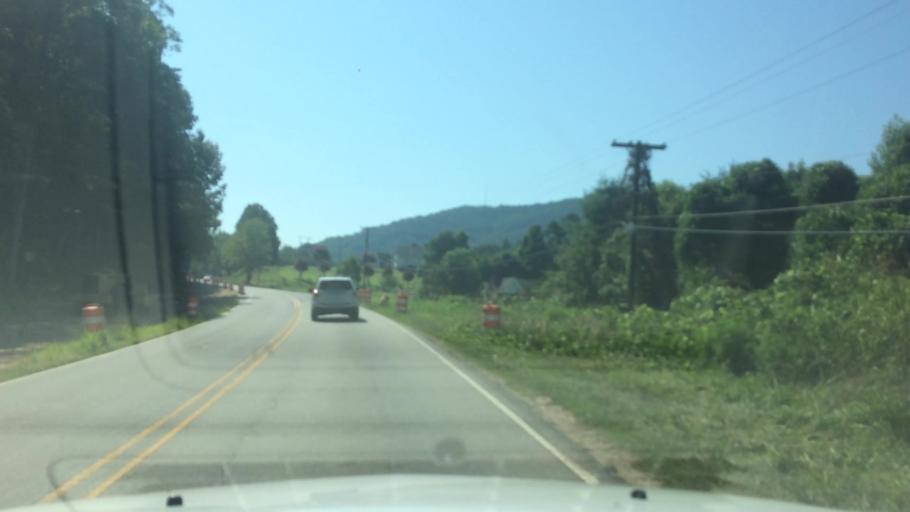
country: US
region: North Carolina
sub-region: Caldwell County
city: Lenoir
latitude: 35.9232
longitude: -81.5028
